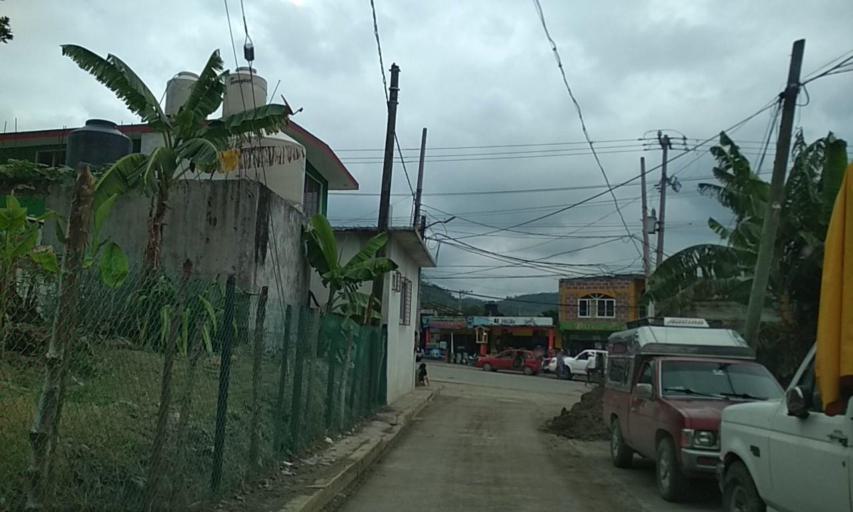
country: MX
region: Veracruz
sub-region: Papantla
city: El Chote
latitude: 20.4006
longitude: -97.3366
